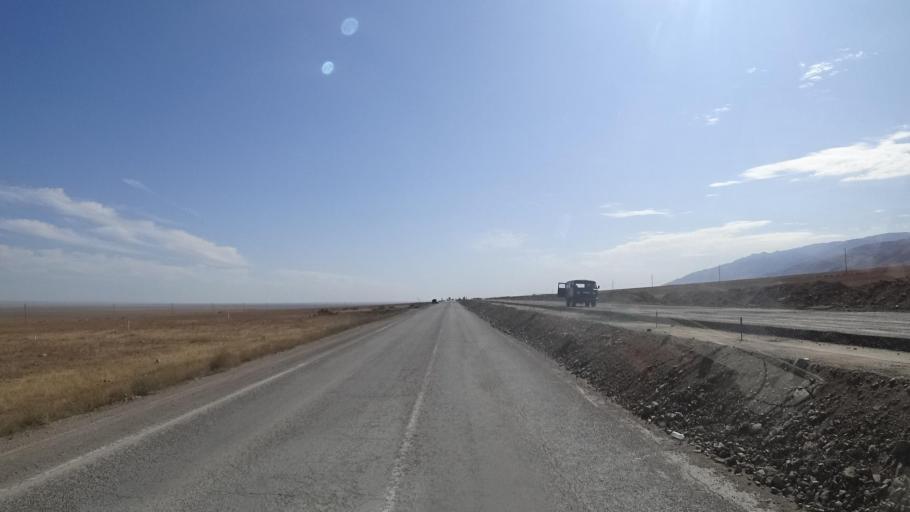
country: KG
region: Chuy
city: Ivanovka
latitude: 43.3839
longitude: 75.1784
